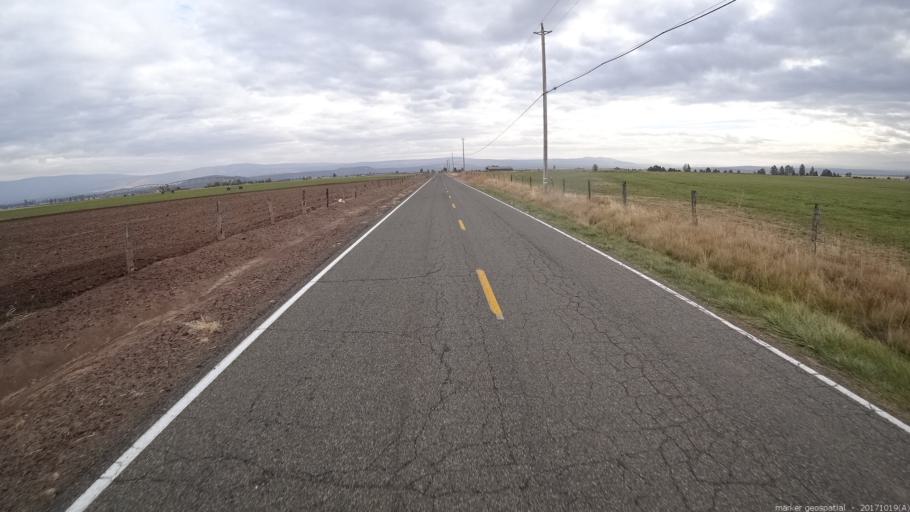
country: US
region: California
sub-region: Shasta County
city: Burney
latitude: 41.0332
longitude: -121.3735
